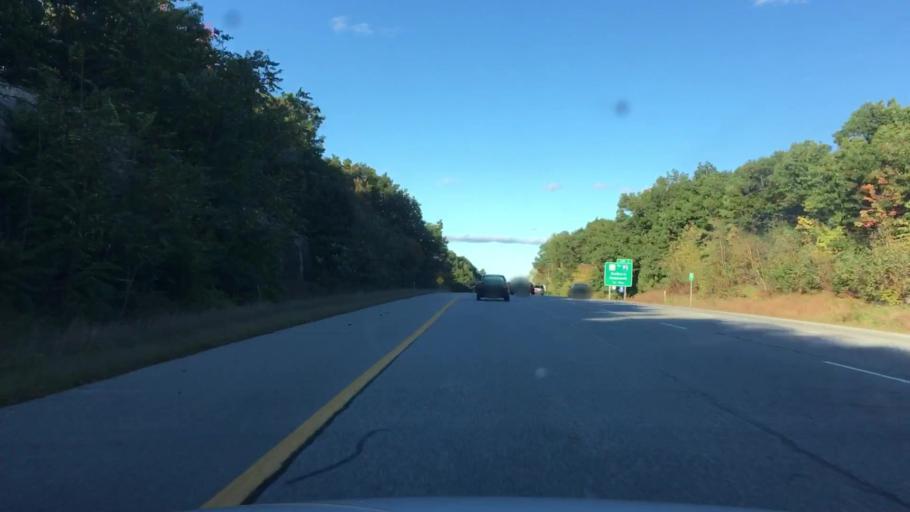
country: US
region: New Hampshire
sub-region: Merrimack County
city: South Hooksett
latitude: 42.9985
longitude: -71.4113
